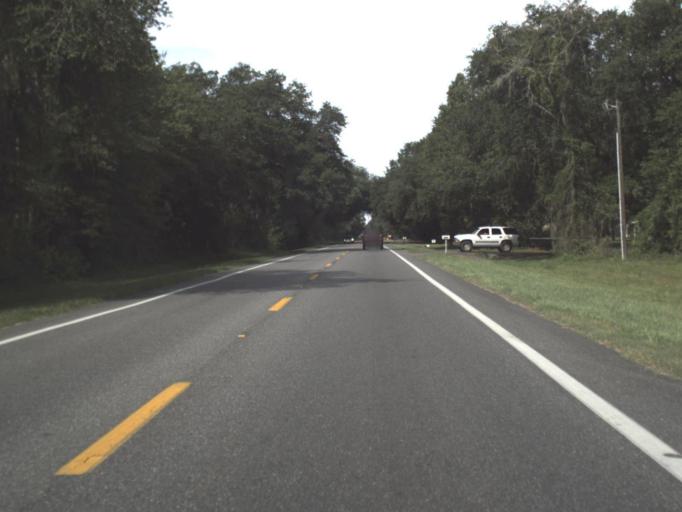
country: US
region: Florida
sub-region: Suwannee County
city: Live Oak
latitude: 30.2683
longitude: -83.0214
